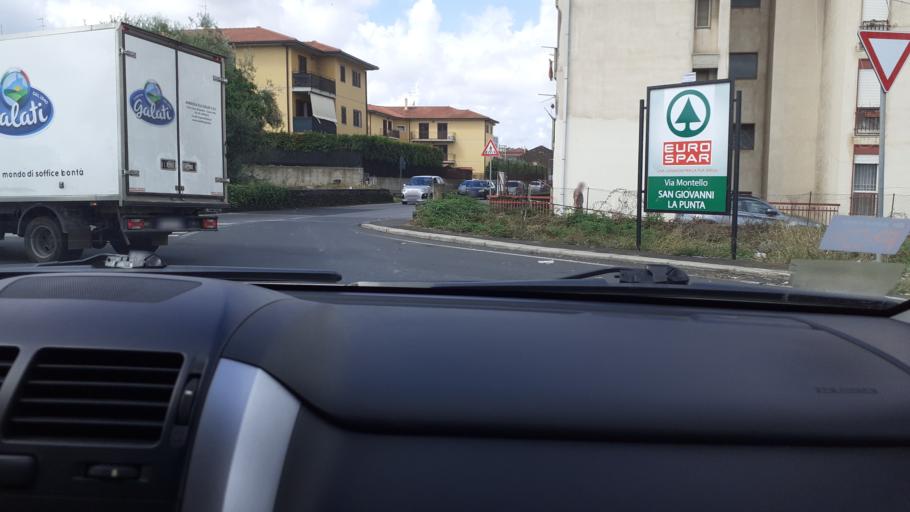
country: IT
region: Sicily
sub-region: Catania
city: San Giovanni la Punta
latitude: 37.5783
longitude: 15.1036
